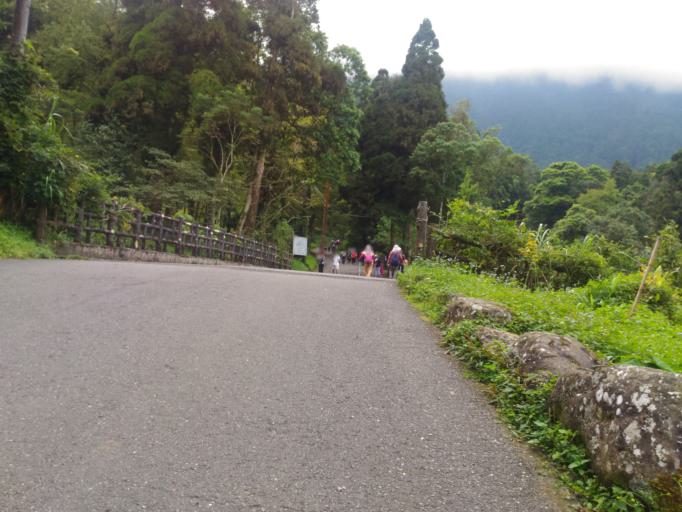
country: TW
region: Taiwan
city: Lugu
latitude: 23.6678
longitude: 120.7981
